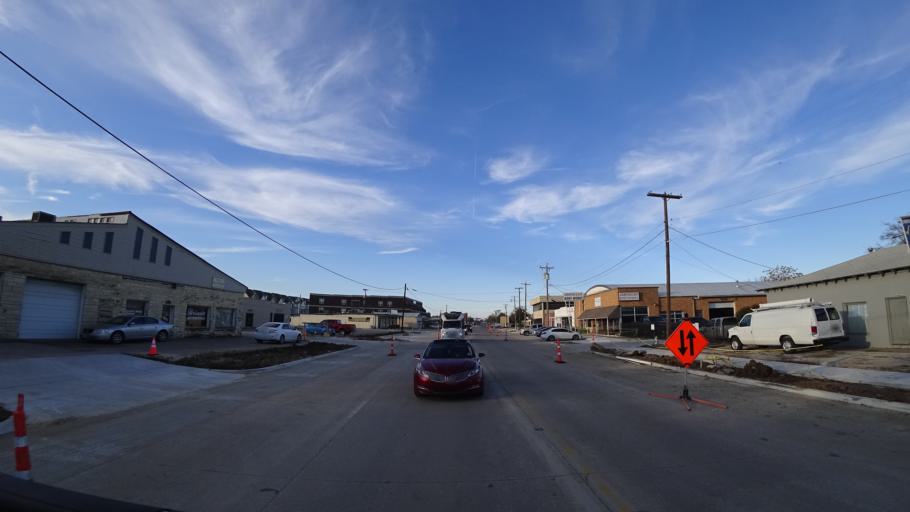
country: US
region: Texas
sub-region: Denton County
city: Lewisville
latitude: 33.0433
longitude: -96.9942
